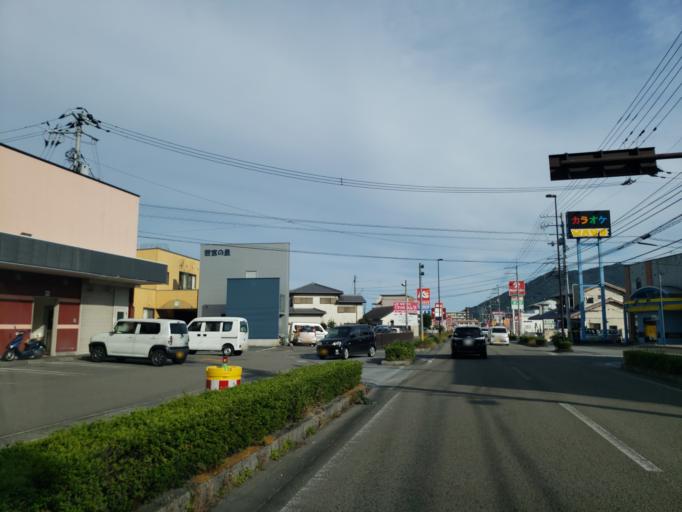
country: JP
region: Tokushima
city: Wakimachi
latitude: 34.0643
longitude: 134.1574
